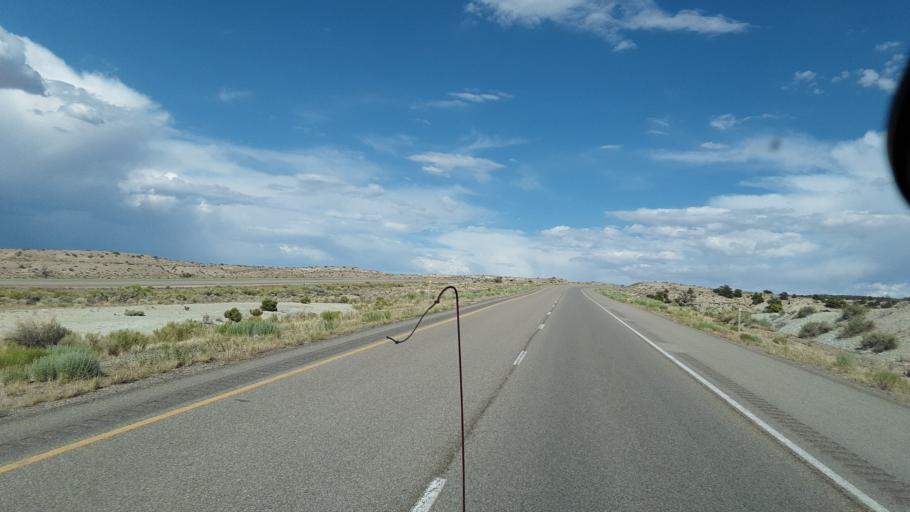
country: US
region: Utah
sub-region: Emery County
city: Ferron
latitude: 38.8430
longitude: -110.9796
